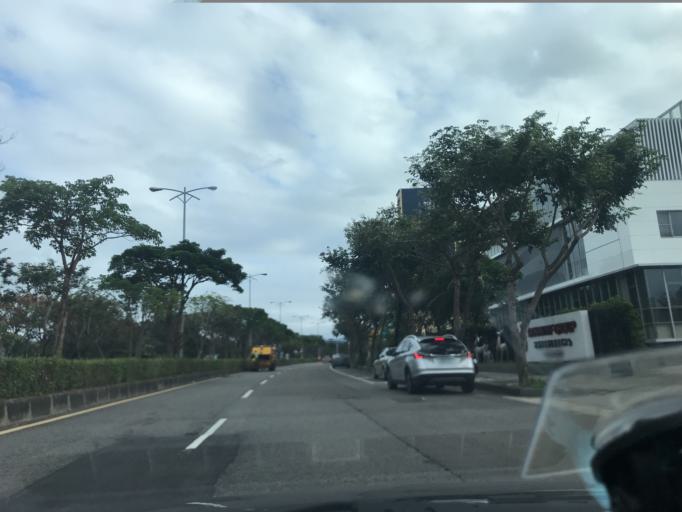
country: TW
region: Taiwan
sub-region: Hsinchu
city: Zhubei
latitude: 24.8053
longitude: 121.0421
